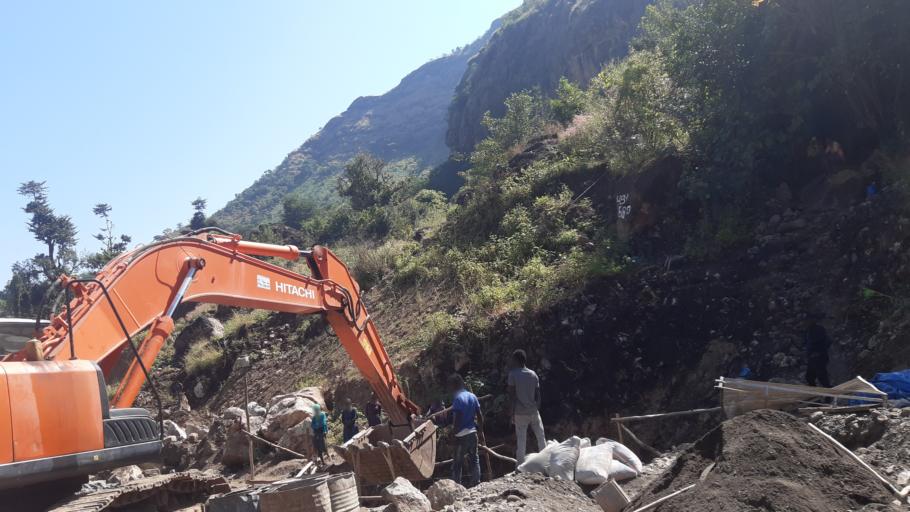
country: ET
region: Amhara
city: Dabat
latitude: 13.1825
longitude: 37.5976
